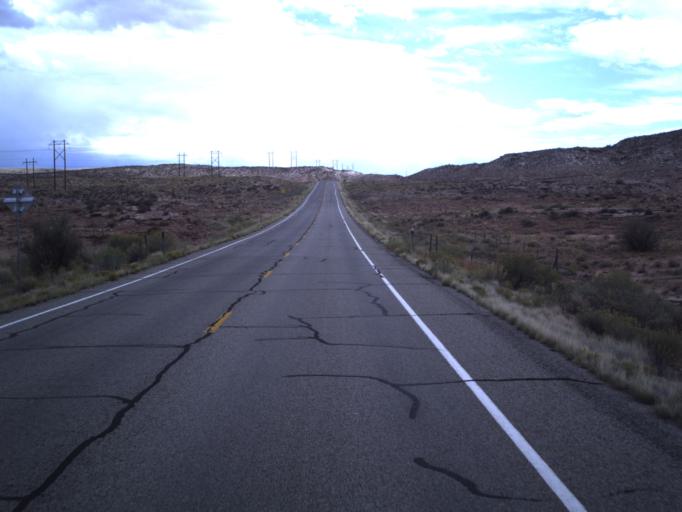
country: US
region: Utah
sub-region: San Juan County
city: Blanding
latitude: 37.2874
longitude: -109.3931
